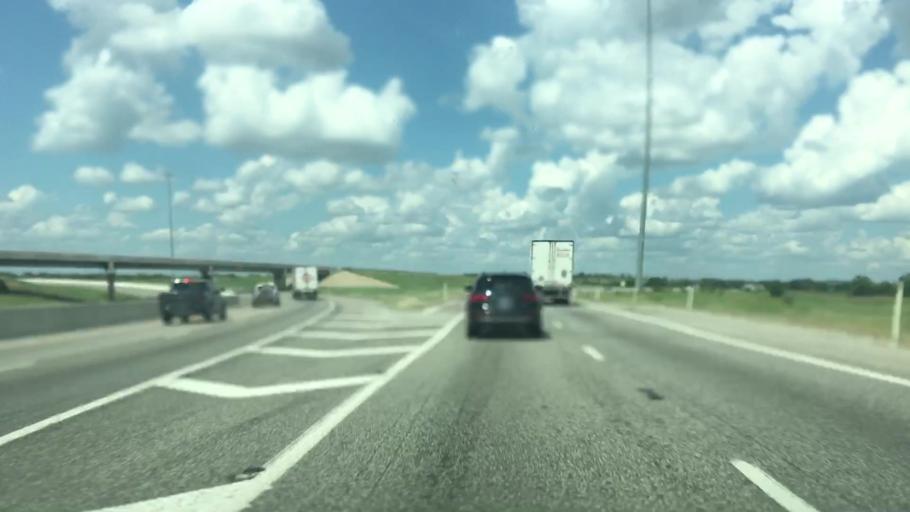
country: US
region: Texas
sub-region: Hill County
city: Hillsboro
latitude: 32.0534
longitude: -97.0933
